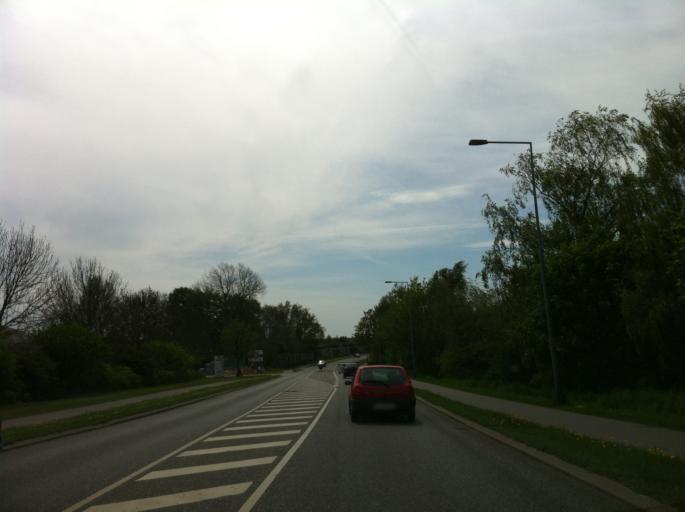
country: DK
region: Zealand
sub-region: Naestved Kommune
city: Naestved
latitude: 55.2199
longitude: 11.7769
